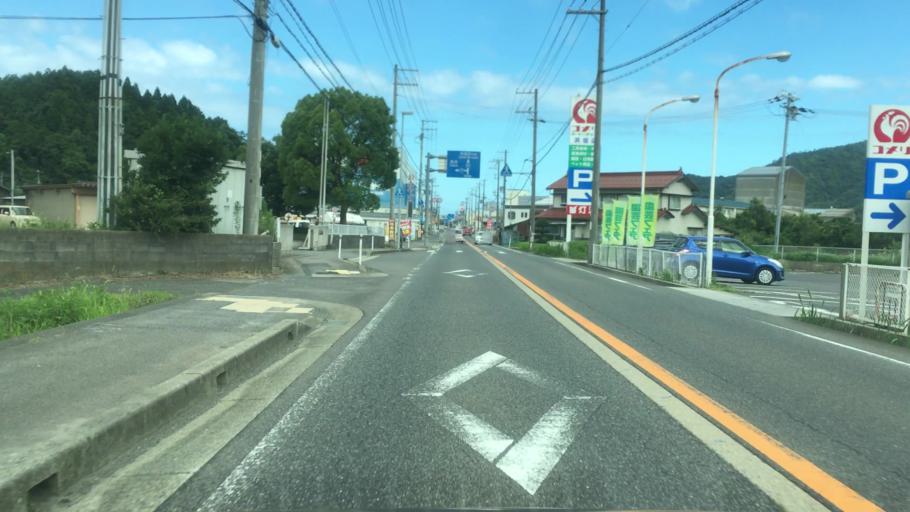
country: JP
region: Tottori
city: Tottori
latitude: 35.6162
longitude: 134.4646
